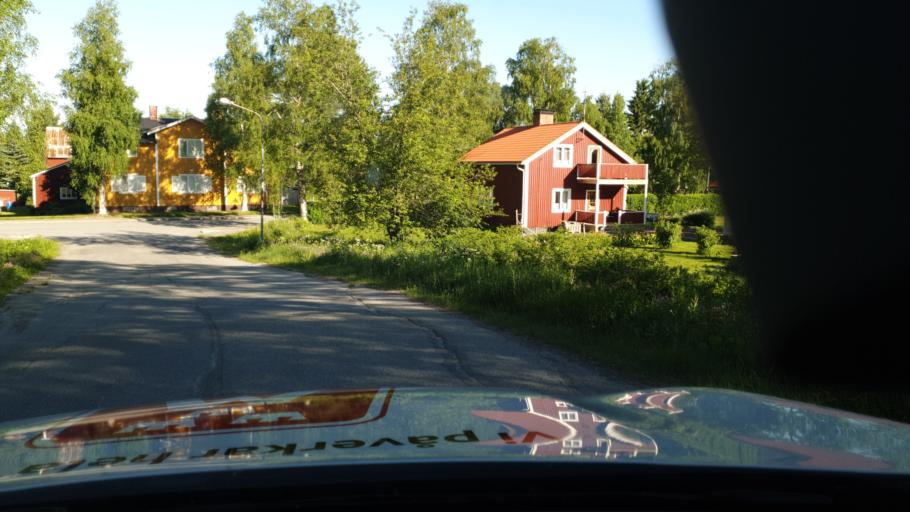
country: SE
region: Vaesterbotten
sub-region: Vindelns Kommun
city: Vindeln
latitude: 64.1965
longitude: 19.7131
